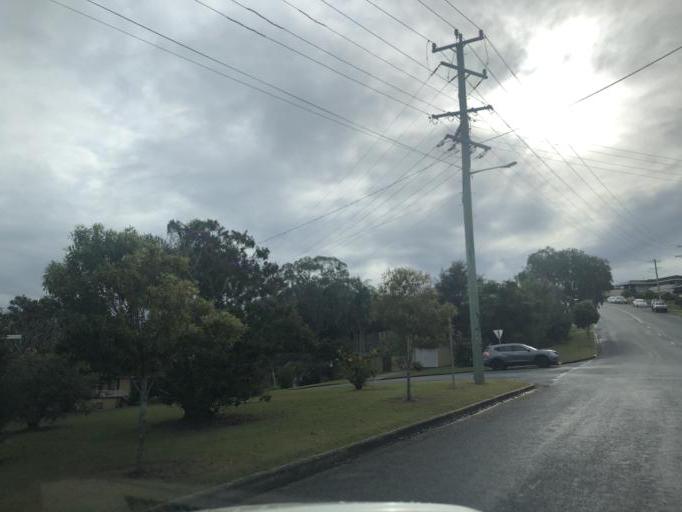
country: AU
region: New South Wales
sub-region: Coffs Harbour
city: Coffs Harbour
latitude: -30.2902
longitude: 153.1131
